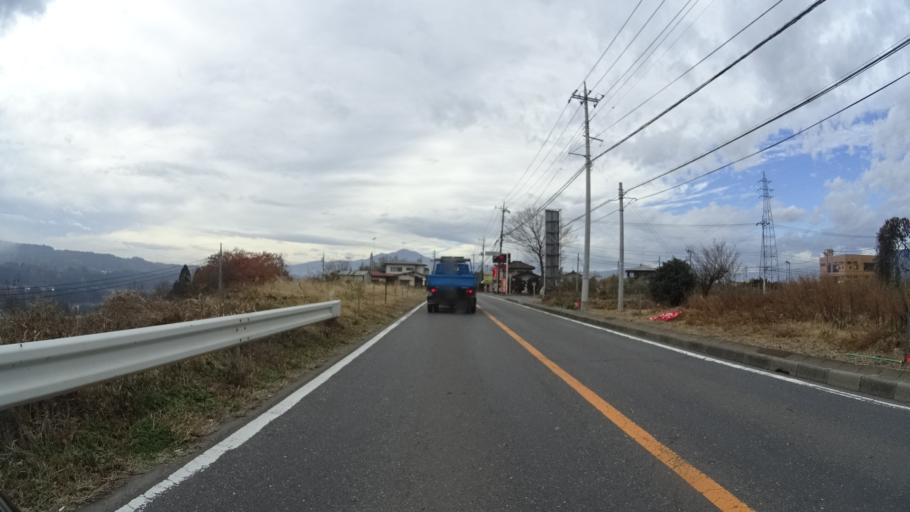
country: JP
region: Gunma
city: Numata
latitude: 36.6624
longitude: 139.0953
